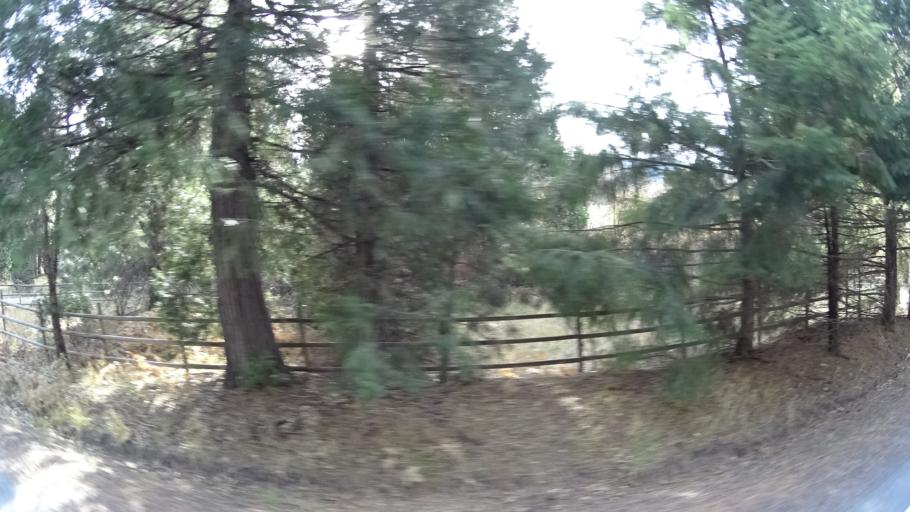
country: US
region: California
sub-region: Siskiyou County
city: Weed
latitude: 41.3973
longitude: -122.4182
